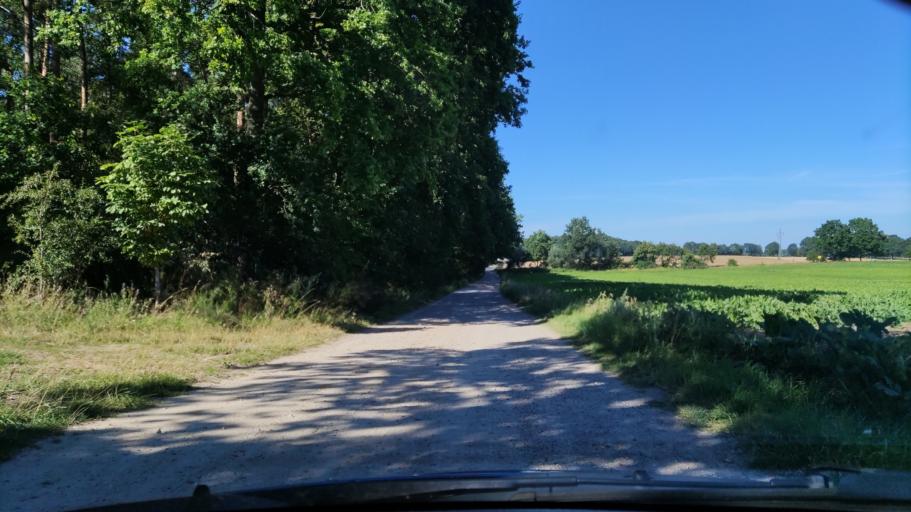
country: DE
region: Lower Saxony
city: Thomasburg
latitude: 53.1846
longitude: 10.6749
